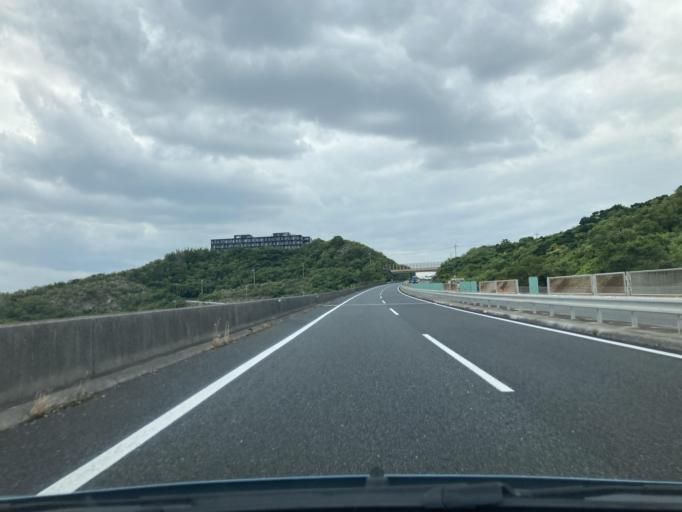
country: JP
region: Okinawa
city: Naha-shi
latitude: 26.2139
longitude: 127.7359
